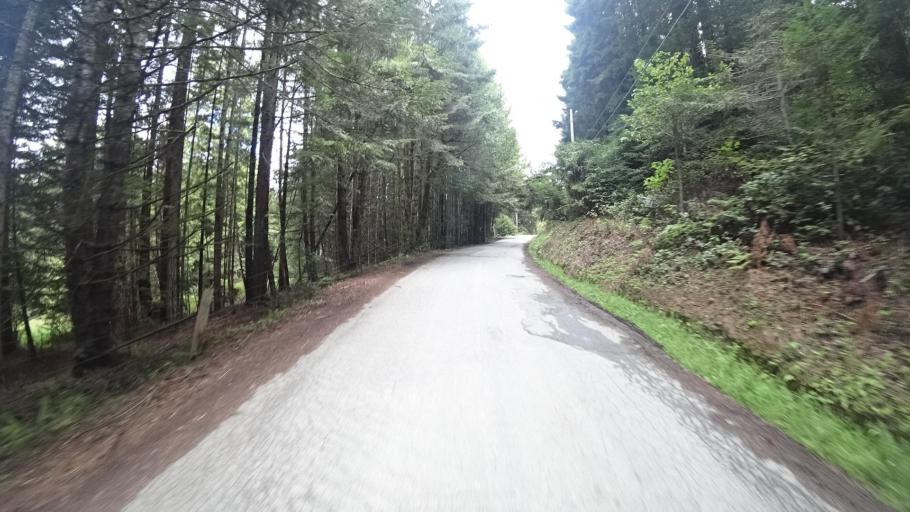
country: US
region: California
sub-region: Humboldt County
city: Blue Lake
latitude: 40.8998
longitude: -123.9920
